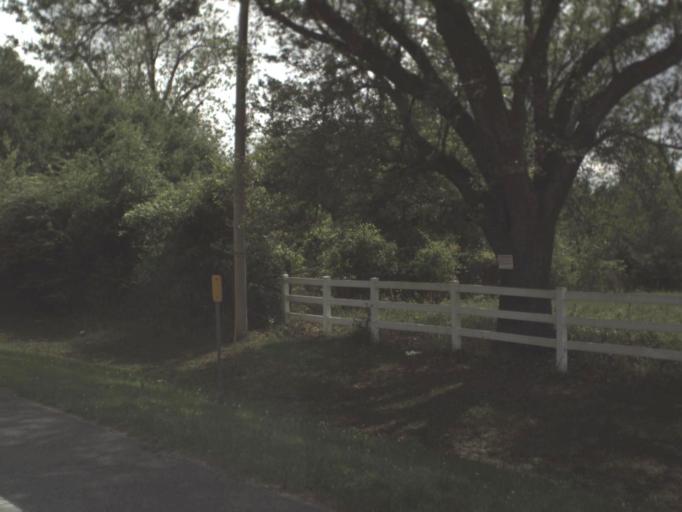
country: US
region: Florida
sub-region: Santa Rosa County
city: Point Baker
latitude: 30.7600
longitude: -87.0931
